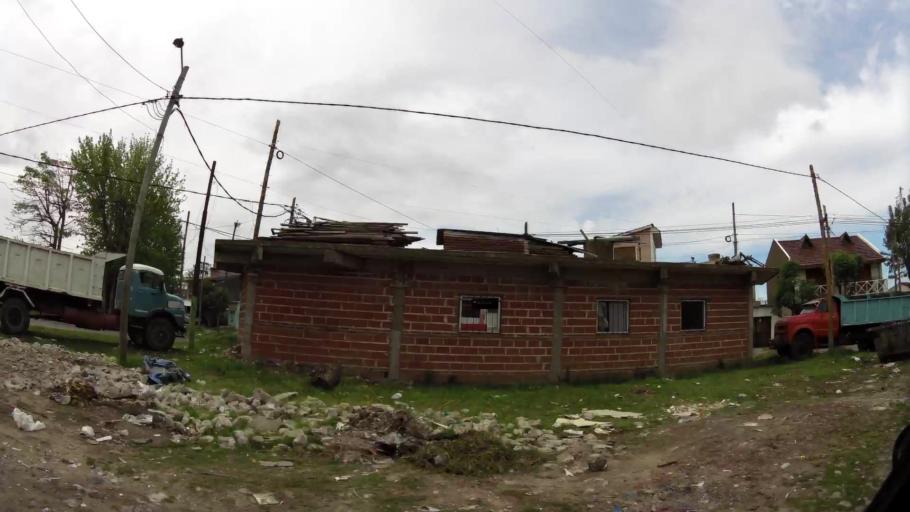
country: AR
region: Buenos Aires
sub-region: Partido de Quilmes
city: Quilmes
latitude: -34.7596
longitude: -58.2638
